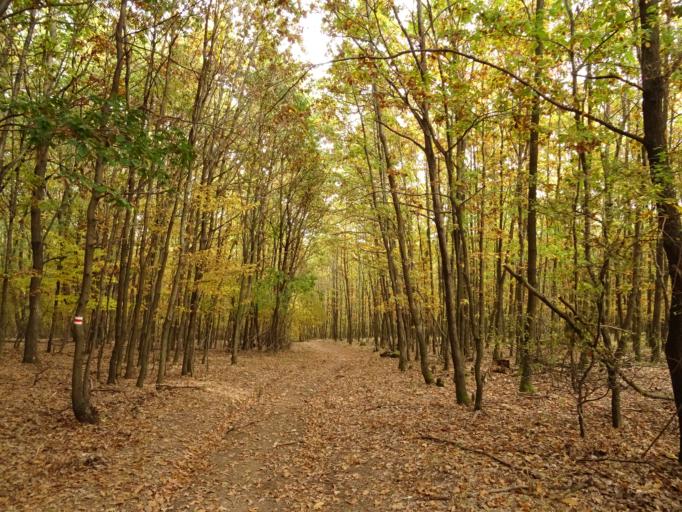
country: HU
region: Heves
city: Gyongyostarjan
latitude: 47.8665
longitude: 19.8913
